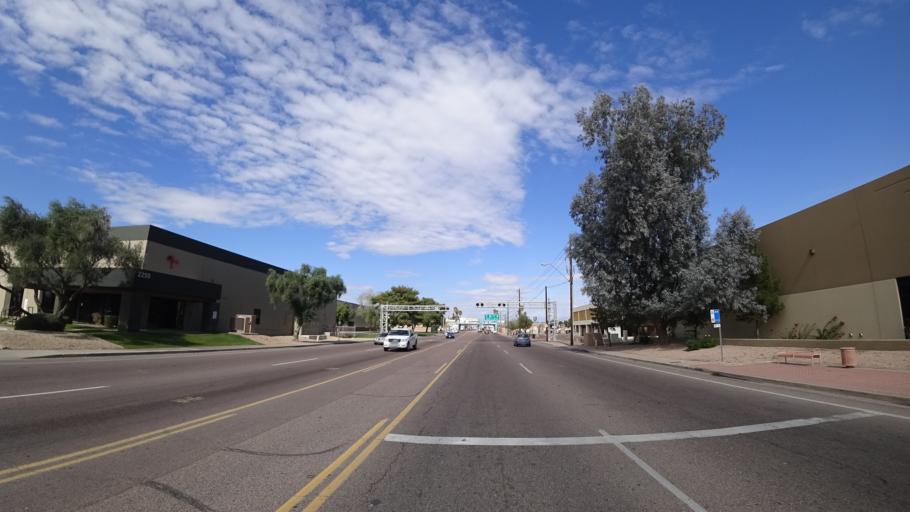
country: US
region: Arizona
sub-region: Maricopa County
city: Phoenix
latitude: 33.4260
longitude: -112.0651
